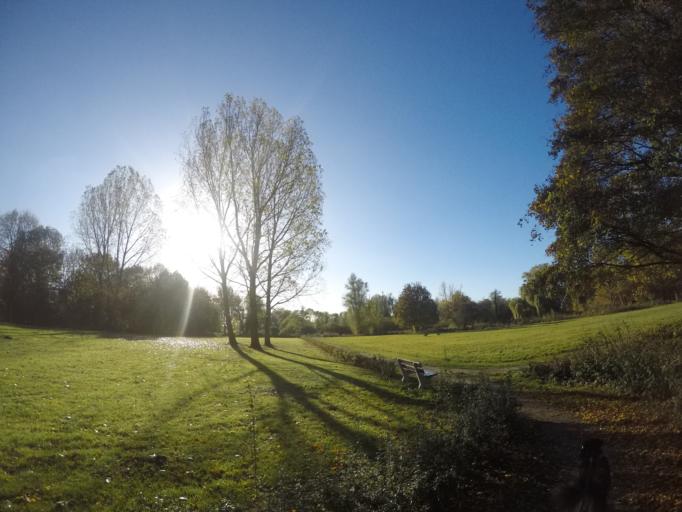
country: NL
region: Gelderland
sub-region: Gemeente Zevenaar
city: Zevenaar
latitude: 51.9190
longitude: 6.0733
